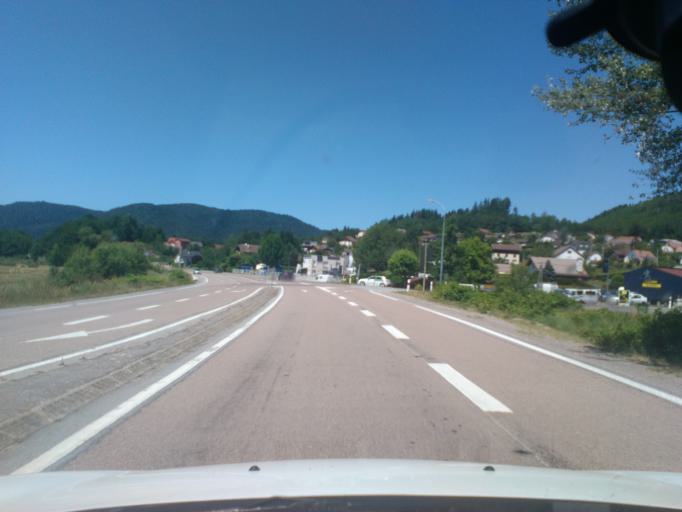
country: FR
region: Lorraine
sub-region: Departement des Vosges
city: Le Syndicat
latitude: 48.0240
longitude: 6.7026
